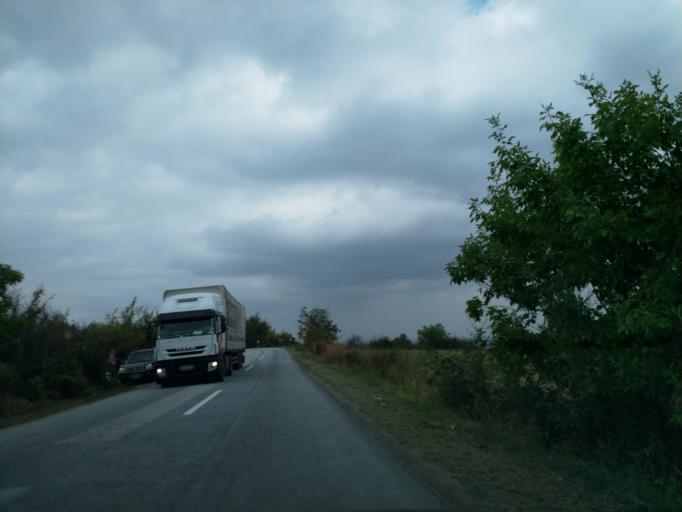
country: RS
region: Central Serbia
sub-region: Sumadijski Okrug
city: Topola
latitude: 44.1515
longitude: 20.7415
